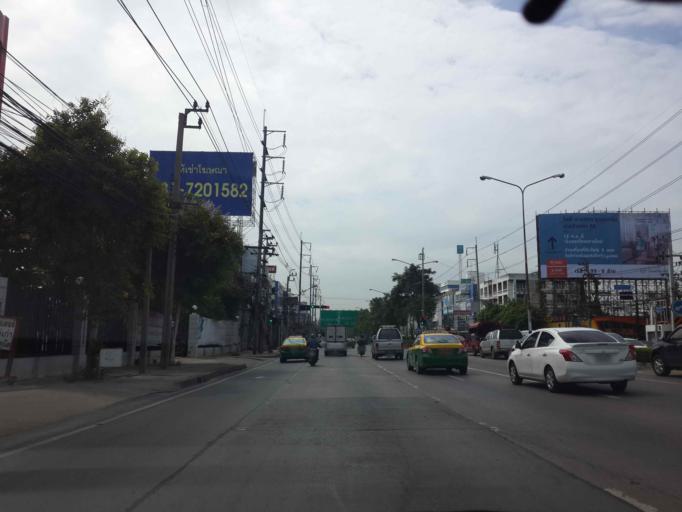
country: TH
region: Bangkok
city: Bang Khen
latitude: 13.8559
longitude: 100.6307
